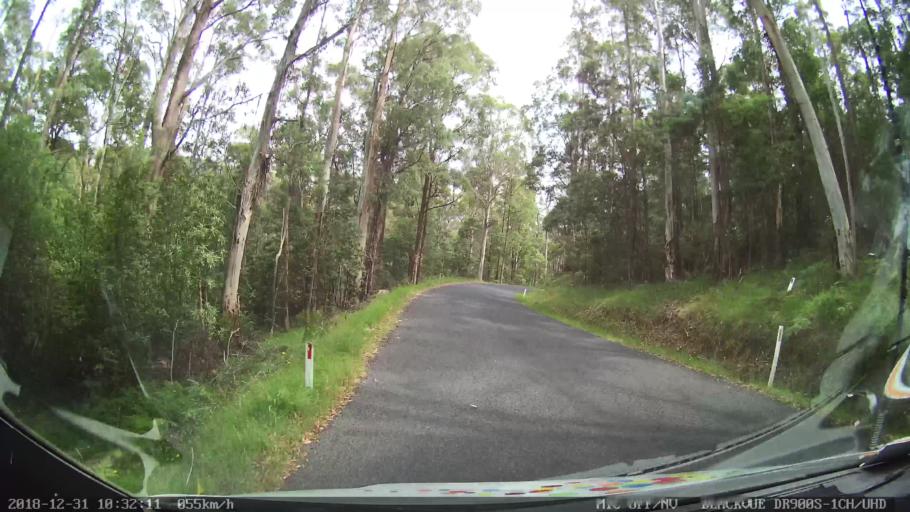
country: AU
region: New South Wales
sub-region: Snowy River
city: Jindabyne
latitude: -36.4525
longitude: 148.1604
